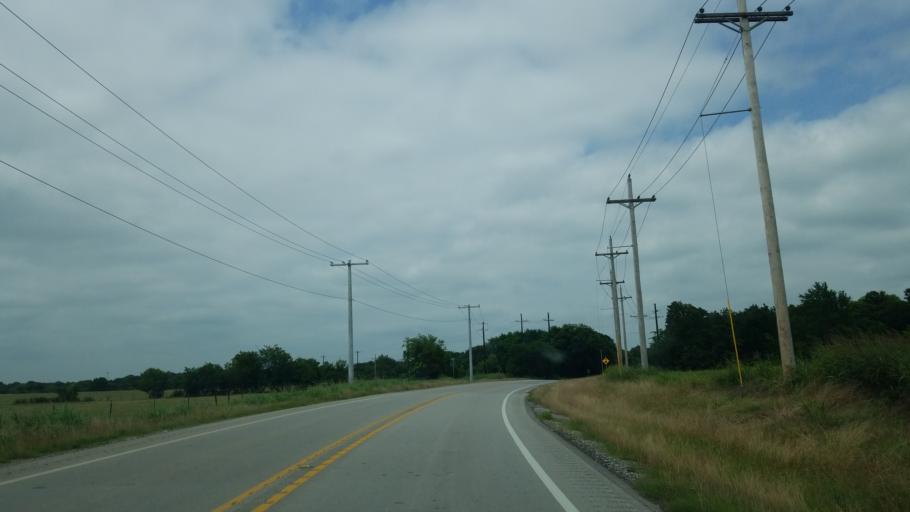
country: US
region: Texas
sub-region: Denton County
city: Aubrey
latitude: 33.3242
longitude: -96.9739
